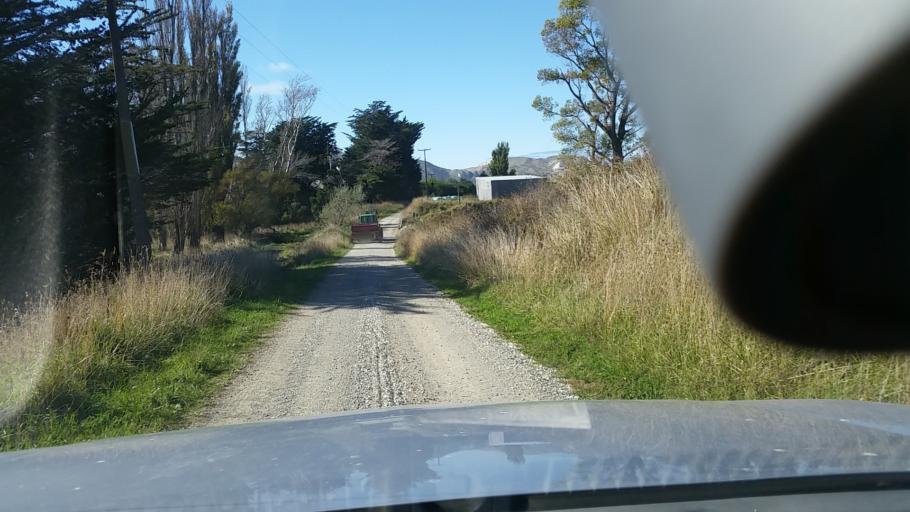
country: NZ
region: Marlborough
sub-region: Marlborough District
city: Blenheim
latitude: -41.8250
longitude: 174.1281
